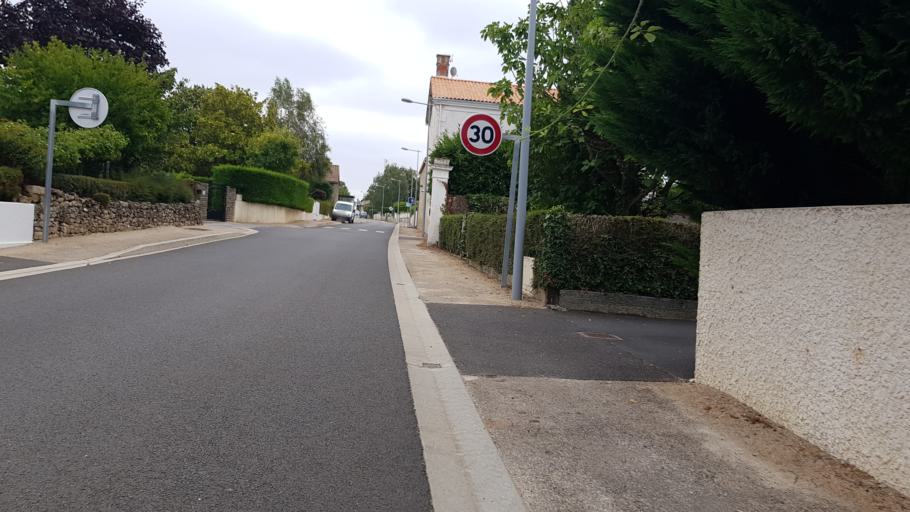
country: FR
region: Poitou-Charentes
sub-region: Departement des Deux-Sevres
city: Vouille
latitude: 46.3246
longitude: -0.3281
